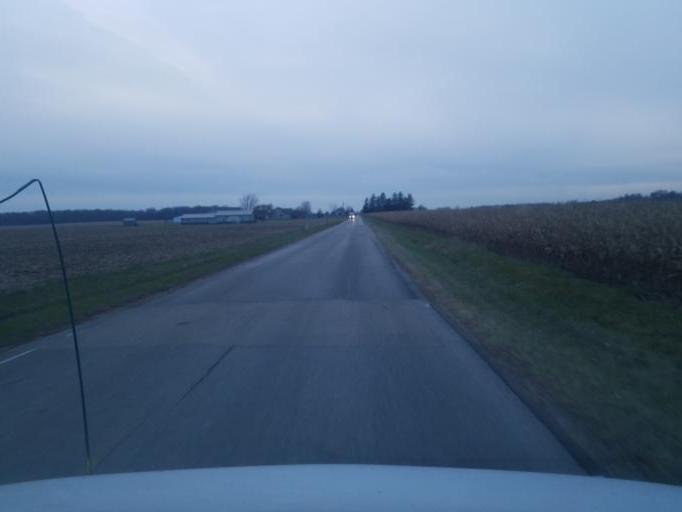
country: US
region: Indiana
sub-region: Adams County
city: Decatur
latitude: 40.7886
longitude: -84.9387
